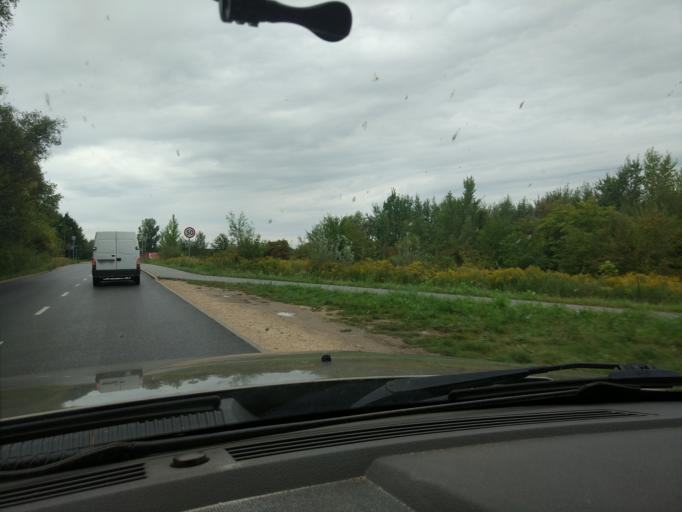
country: PL
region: Masovian Voivodeship
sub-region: Powiat pruszkowski
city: Brwinow
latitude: 52.1735
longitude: 20.7502
